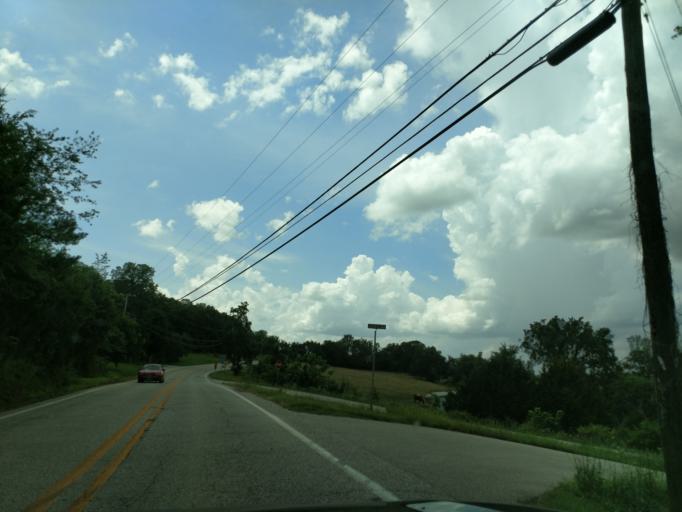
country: US
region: Arkansas
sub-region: Boone County
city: Harrison
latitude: 36.2473
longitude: -93.2118
